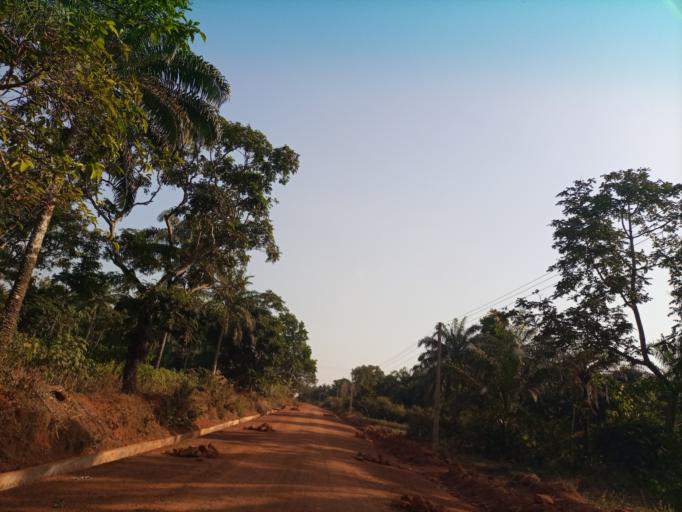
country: NG
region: Enugu
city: Opi
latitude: 6.7728
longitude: 7.3908
